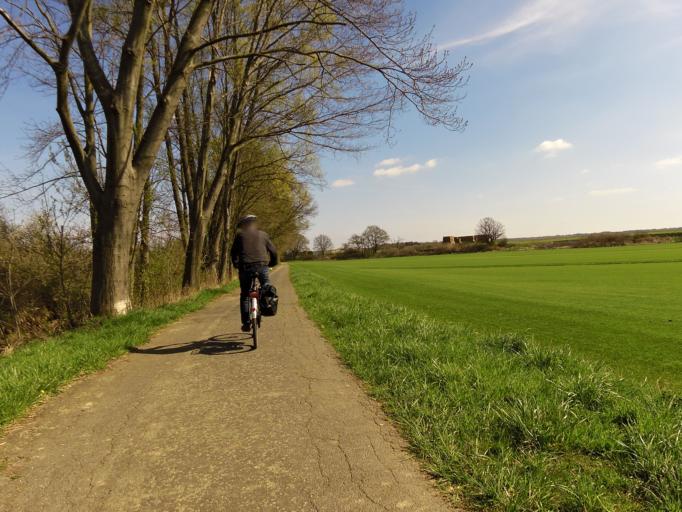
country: DE
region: North Rhine-Westphalia
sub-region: Regierungsbezirk Koln
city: Rheinbach
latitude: 50.6882
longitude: 6.9245
